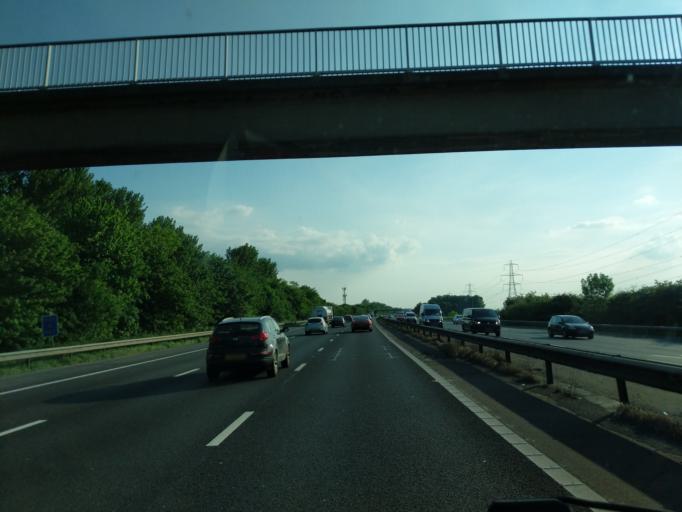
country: GB
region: England
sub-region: Cheshire West and Chester
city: Helsby
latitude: 53.2805
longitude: -2.7663
